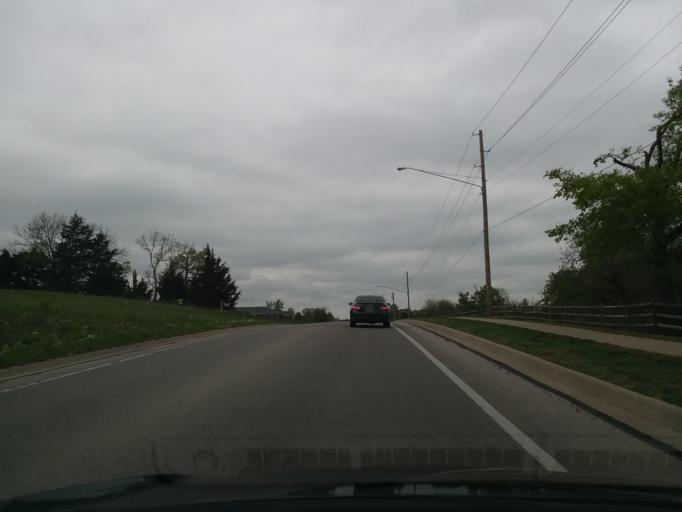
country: US
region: Kansas
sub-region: Douglas County
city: Lawrence
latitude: 38.9830
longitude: -95.2882
